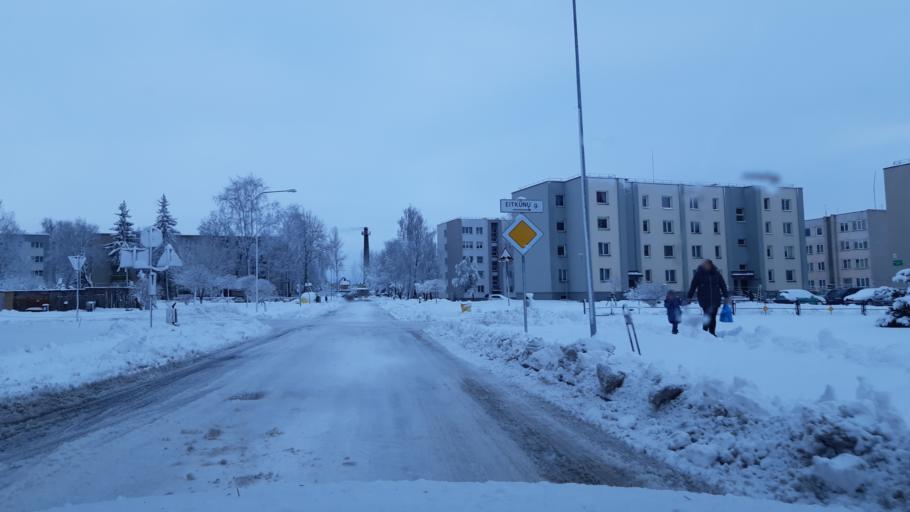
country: LT
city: Kybartai
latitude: 54.6358
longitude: 22.7560
